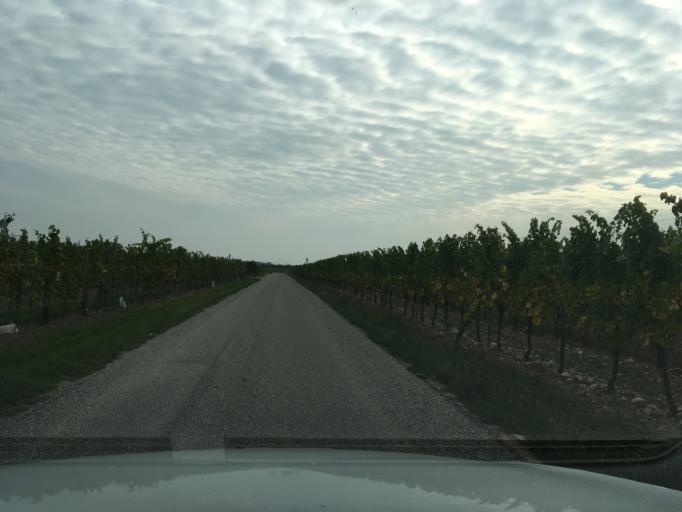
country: FR
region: Alsace
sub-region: Departement du Haut-Rhin
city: Colmar
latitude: 48.0968
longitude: 7.3433
